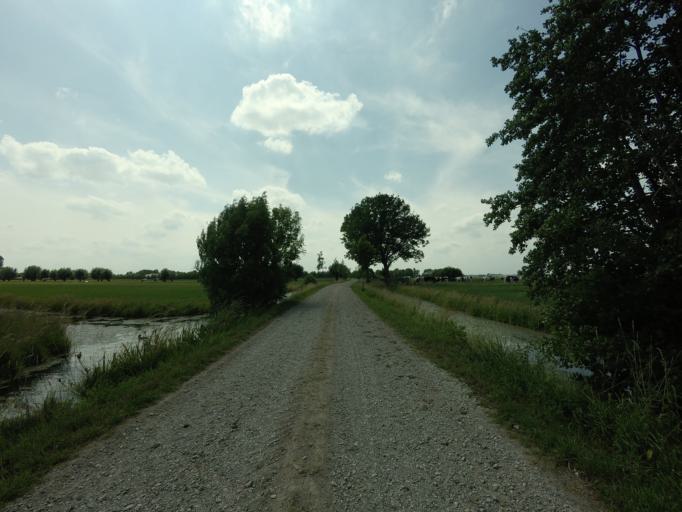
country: NL
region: Utrecht
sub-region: Gemeente Lopik
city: Lopik
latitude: 51.9506
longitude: 4.9148
